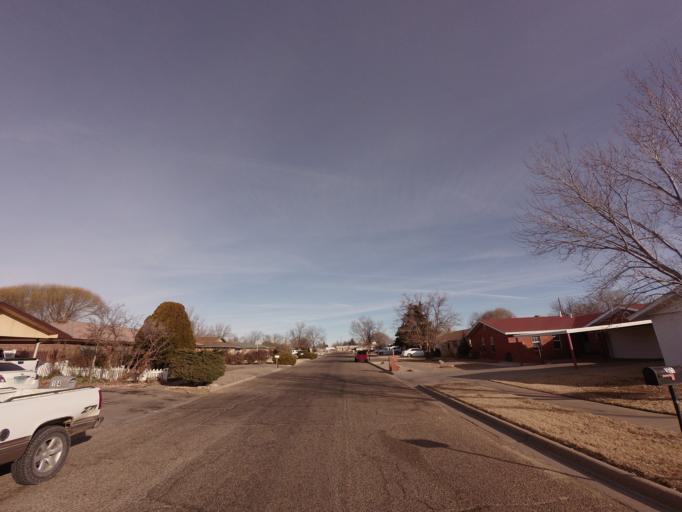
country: US
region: New Mexico
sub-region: Curry County
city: Clovis
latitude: 34.4162
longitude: -103.2239
